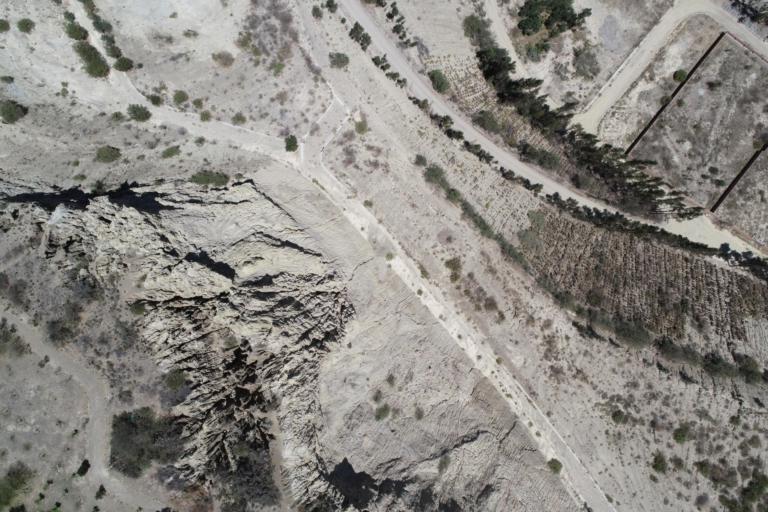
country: BO
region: La Paz
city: La Paz
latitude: -16.6229
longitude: -68.0599
